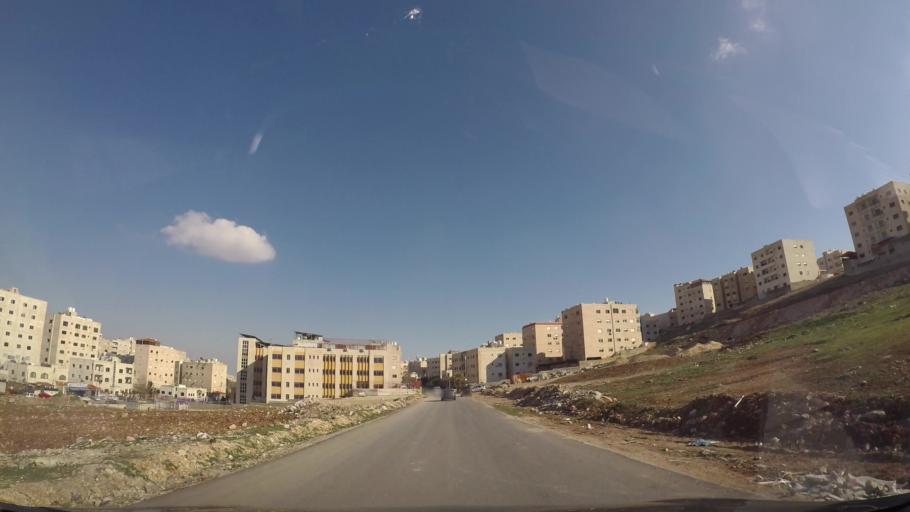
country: JO
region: Amman
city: Amman
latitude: 31.9764
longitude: 35.9358
